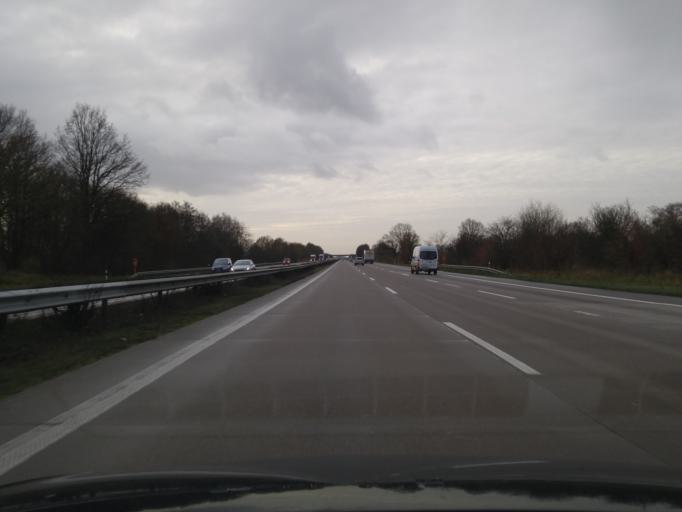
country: DE
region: Schleswig-Holstein
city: Lasbek
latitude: 53.7417
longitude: 10.3591
